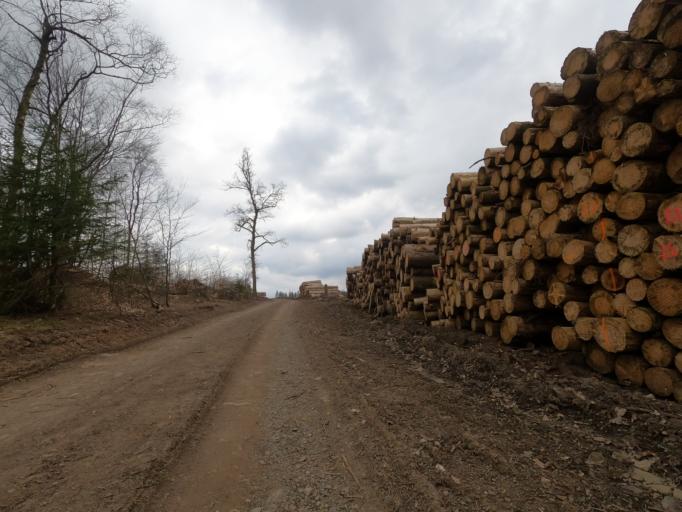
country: DE
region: North Rhine-Westphalia
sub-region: Regierungsbezirk Arnsberg
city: Herscheid
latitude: 51.1673
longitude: 7.7386
